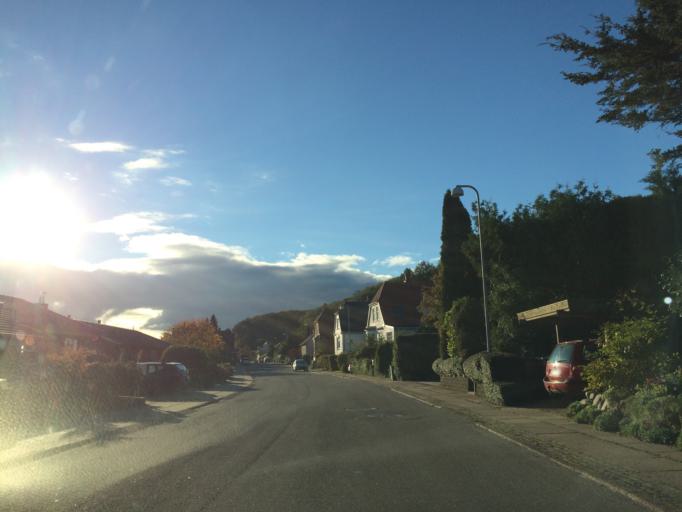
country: DK
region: Central Jutland
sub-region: Skanderborg Kommune
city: Ry
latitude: 56.1265
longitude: 9.7229
